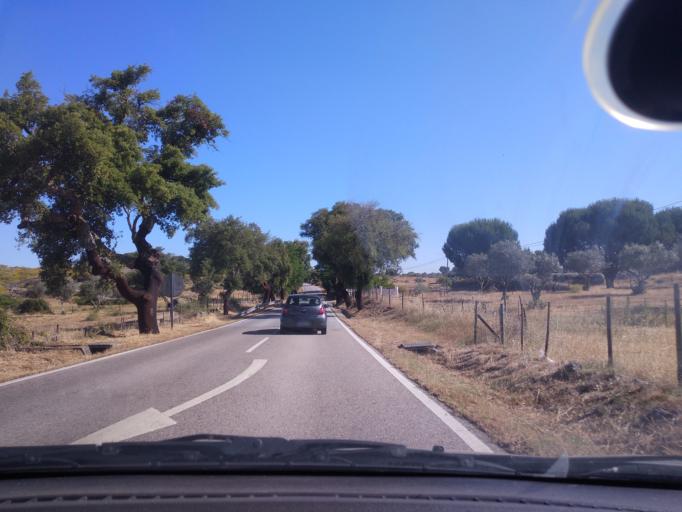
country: PT
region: Portalegre
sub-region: Nisa
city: Nisa
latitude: 39.4826
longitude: -7.6361
